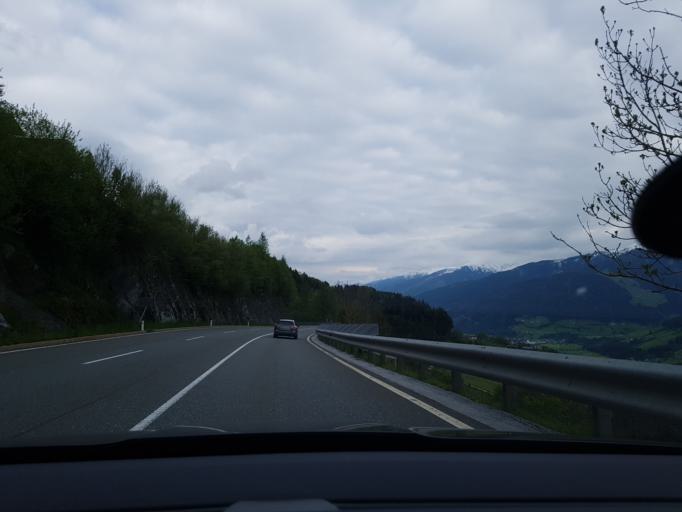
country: AT
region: Salzburg
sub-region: Politischer Bezirk Zell am See
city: Hollersbach im Pinzgau
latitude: 47.2943
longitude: 12.4329
